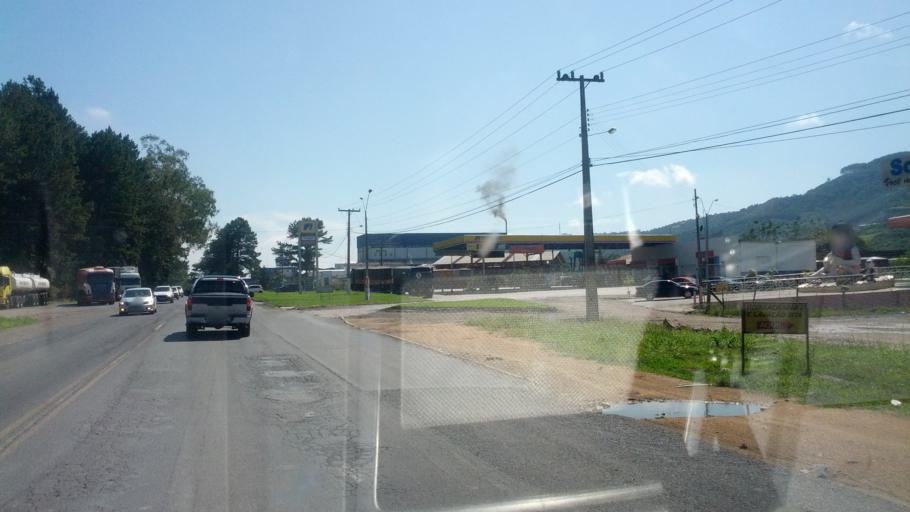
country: BR
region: Santa Catarina
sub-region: Rio Do Sul
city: Rio do Sul
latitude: -27.2430
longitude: -49.6893
